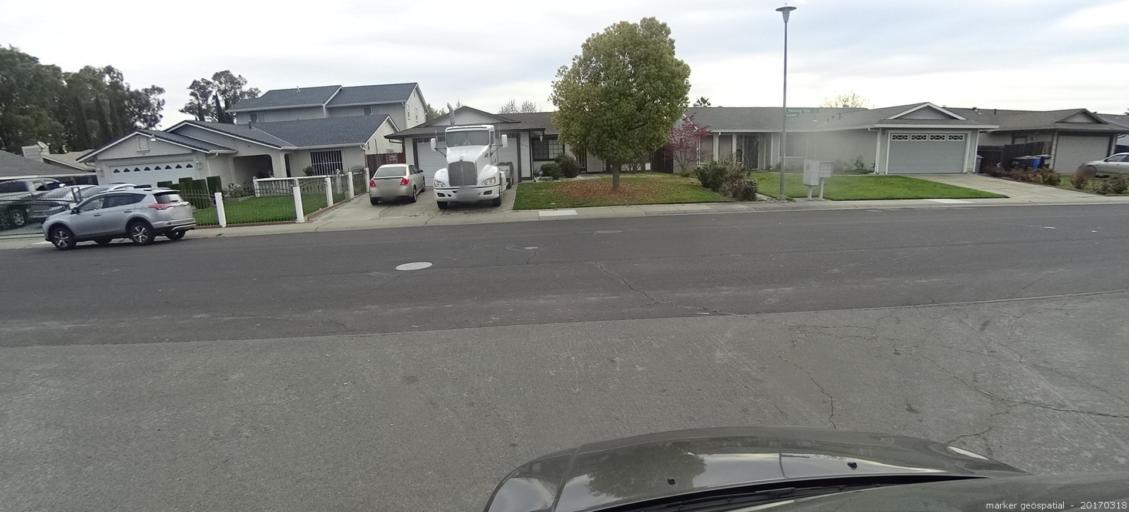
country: US
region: California
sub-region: Sacramento County
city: Parkway
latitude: 38.4840
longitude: -121.4656
